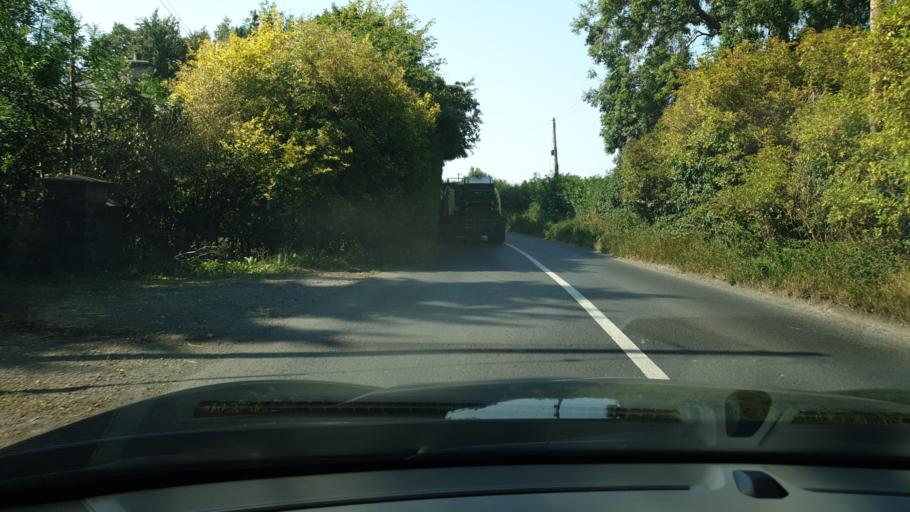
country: IE
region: Leinster
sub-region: An Mhi
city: Athboy
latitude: 53.6185
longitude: -6.9085
